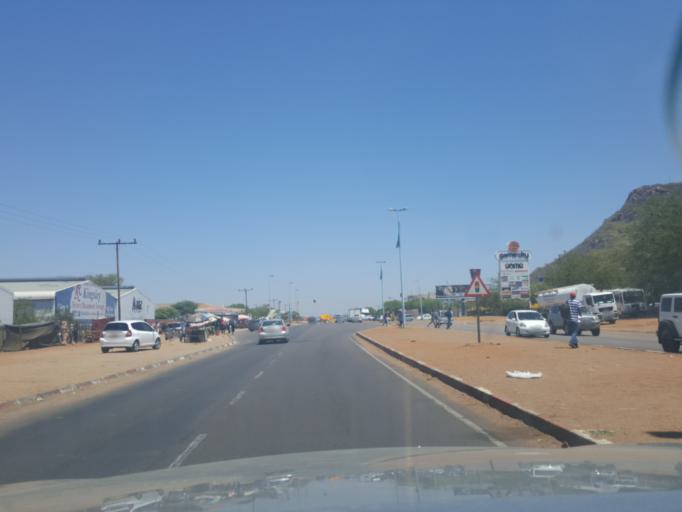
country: BW
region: South East
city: Gaborone
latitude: -24.6886
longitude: 25.8824
